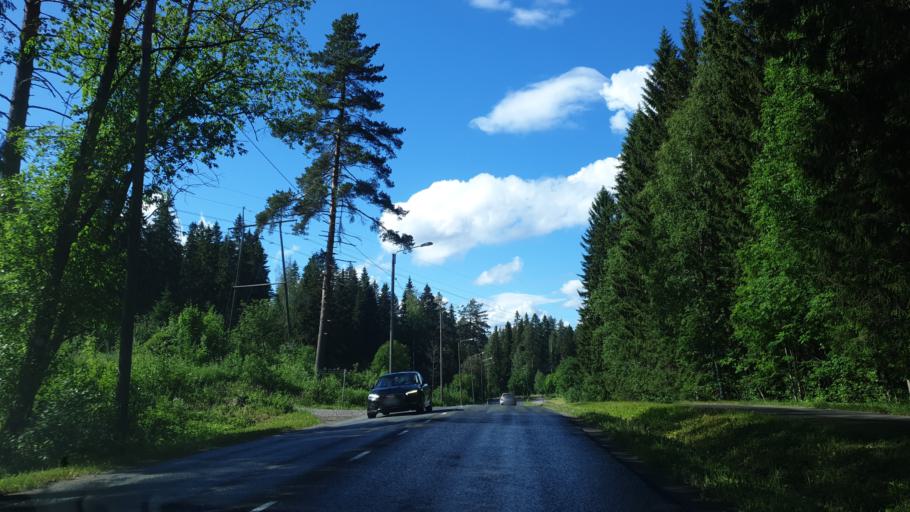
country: FI
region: Northern Savo
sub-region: Kuopio
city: Kuopio
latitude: 62.9114
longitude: 27.6411
